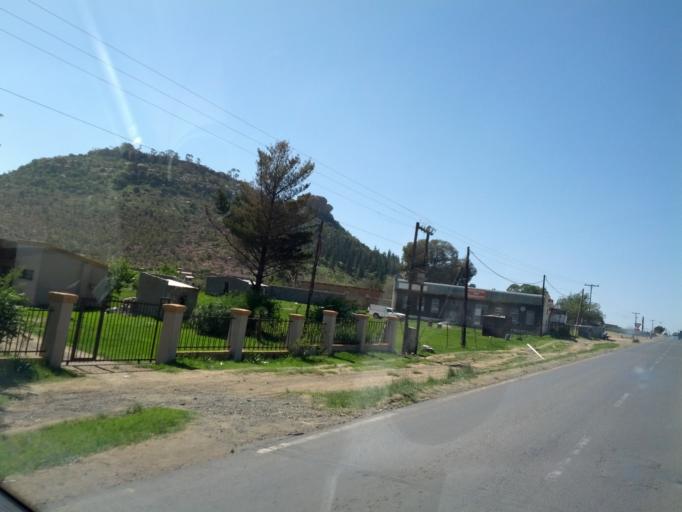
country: LS
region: Maseru
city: Maseru
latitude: -29.3625
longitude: 27.5298
